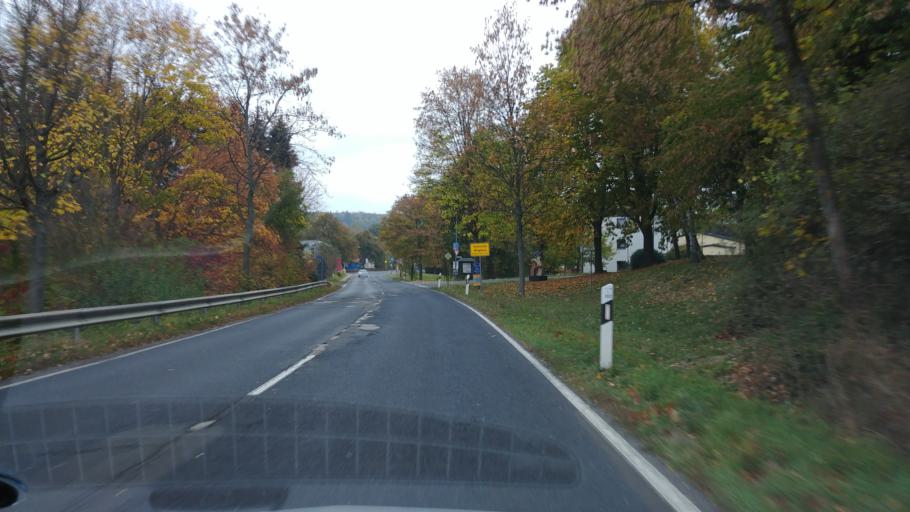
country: DE
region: Hesse
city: Taunusstein
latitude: 50.1649
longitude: 8.1504
